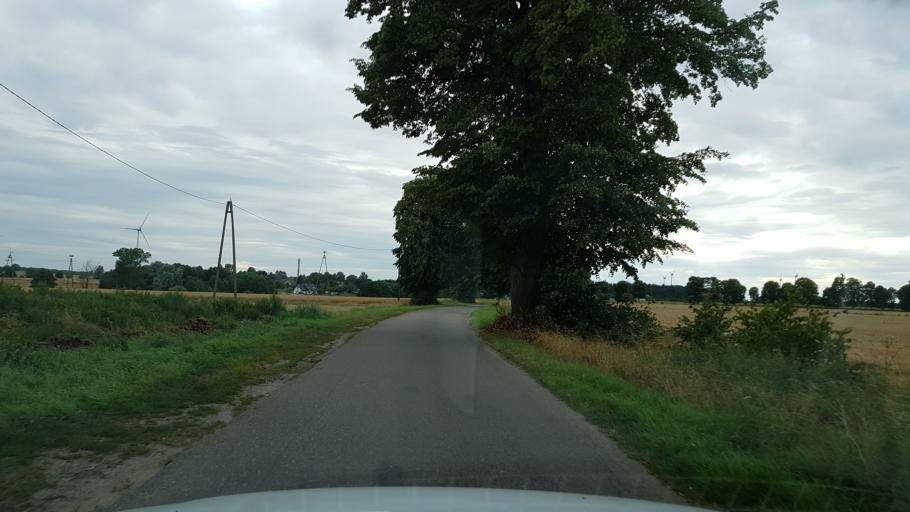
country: PL
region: West Pomeranian Voivodeship
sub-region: Powiat bialogardzki
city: Karlino
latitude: 54.1157
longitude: 15.8526
